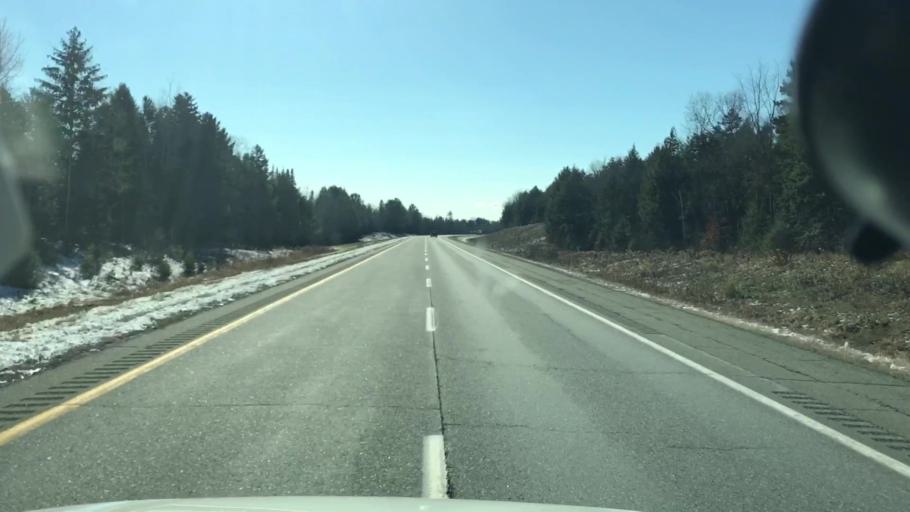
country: US
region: Maine
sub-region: Penobscot County
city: Howland
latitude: 45.2934
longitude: -68.6649
